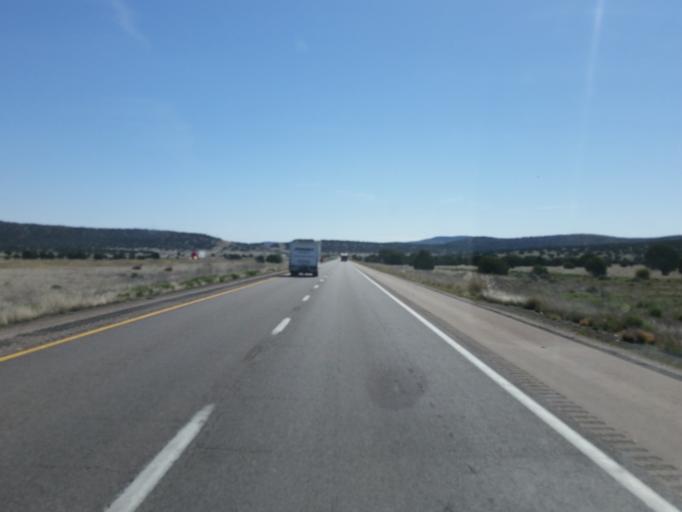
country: US
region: Arizona
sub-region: Mohave County
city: Peach Springs
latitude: 35.2278
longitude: -113.2297
